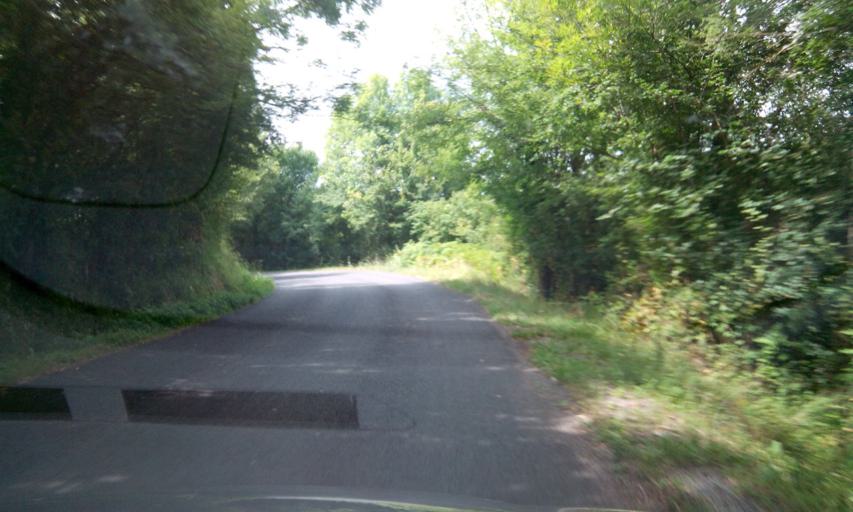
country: FR
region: Limousin
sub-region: Departement de la Correze
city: Meyssac
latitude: 45.0562
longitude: 1.6311
